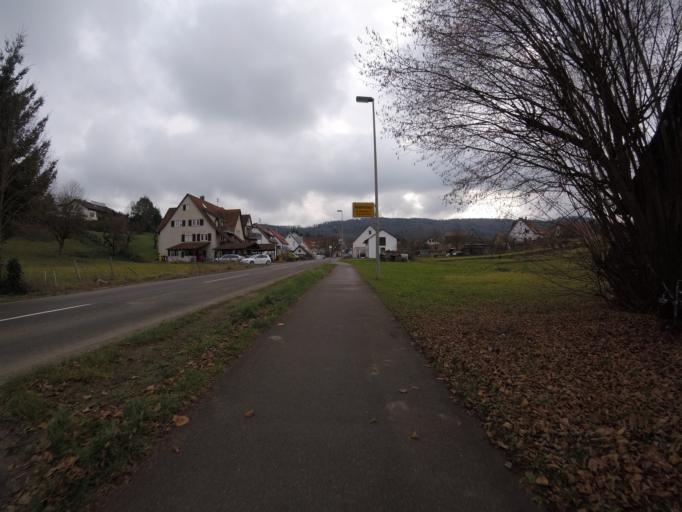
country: DE
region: Baden-Wuerttemberg
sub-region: Regierungsbezirk Stuttgart
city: Allmersbach im Tal
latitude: 48.9100
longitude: 9.4842
